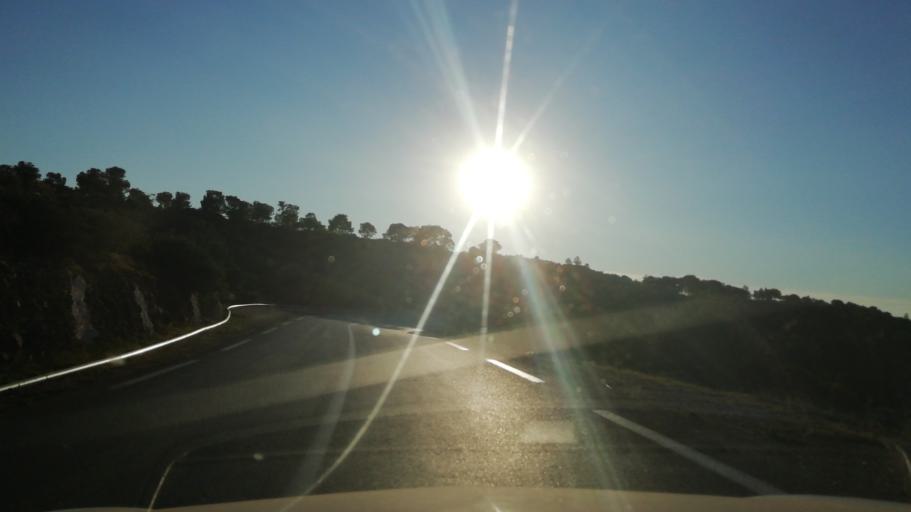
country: DZ
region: Tlemcen
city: Beni Mester
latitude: 34.8130
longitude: -1.6236
